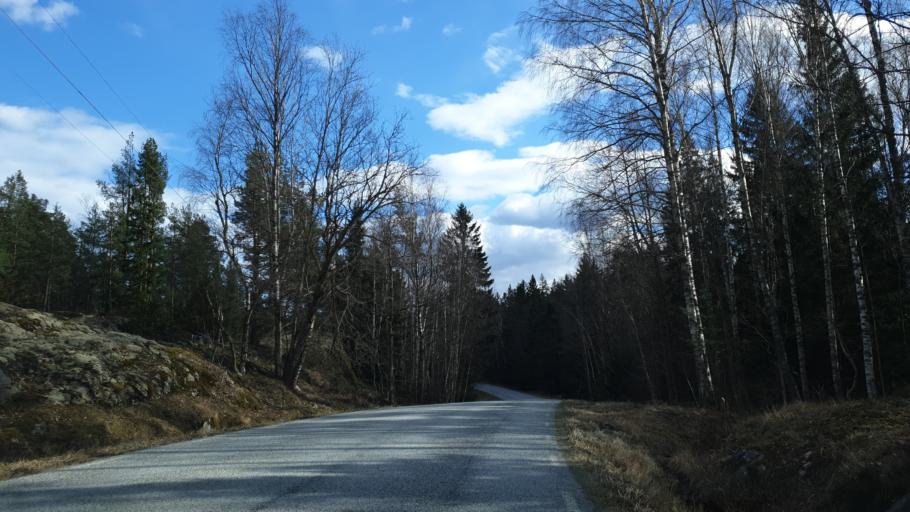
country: SE
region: Stockholm
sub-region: Varmdo Kommun
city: Hemmesta
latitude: 59.2397
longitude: 18.4764
